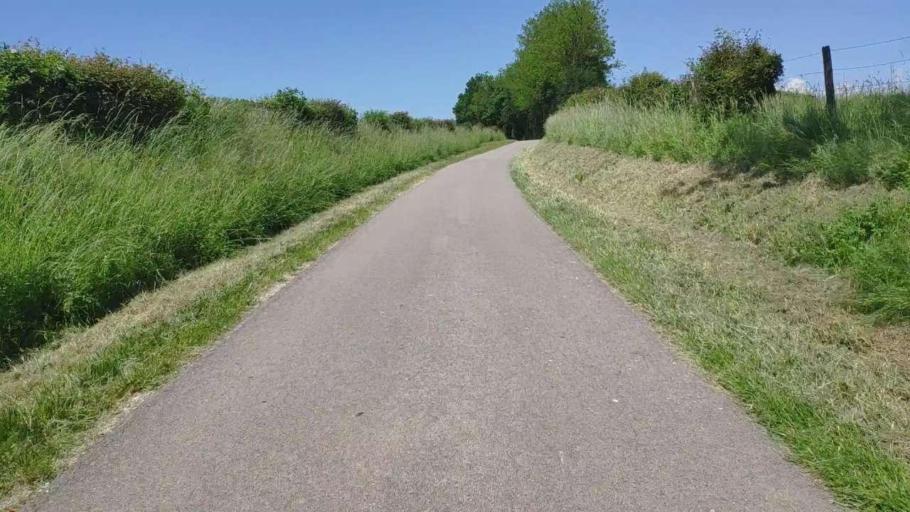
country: FR
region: Franche-Comte
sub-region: Departement du Jura
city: Bletterans
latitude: 46.7517
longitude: 5.3732
